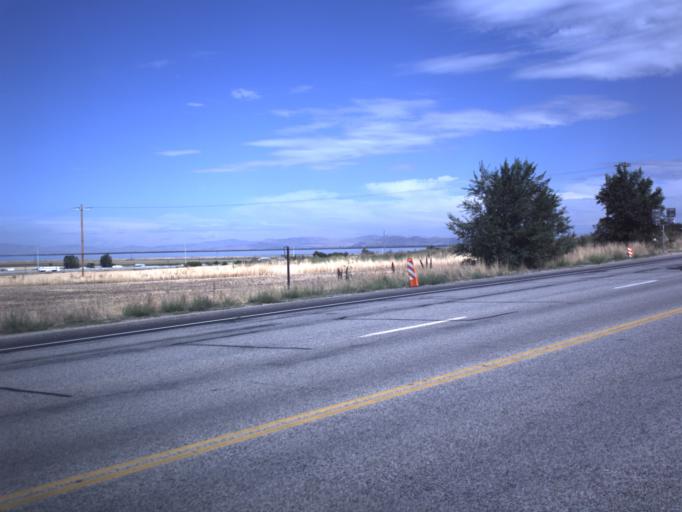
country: US
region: Utah
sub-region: Box Elder County
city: South Willard
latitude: 41.3551
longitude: -112.0357
